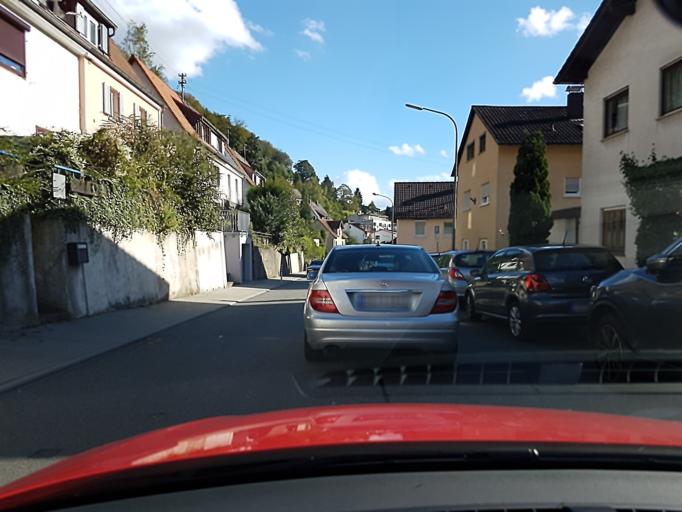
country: DE
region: Baden-Wuerttemberg
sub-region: Karlsruhe Region
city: Wilhelmsfeld
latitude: 49.4314
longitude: 8.7478
